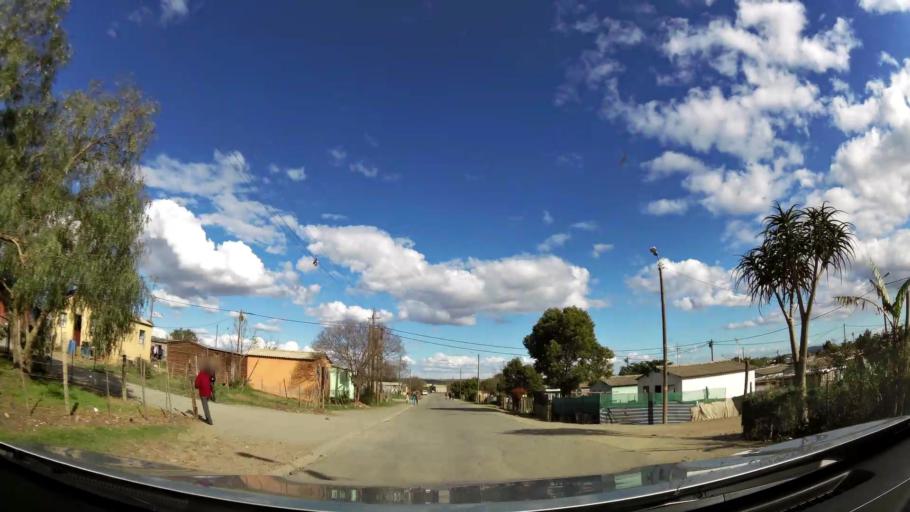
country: ZA
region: Western Cape
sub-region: Overberg District Municipality
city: Swellendam
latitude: -34.0444
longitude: 20.4452
